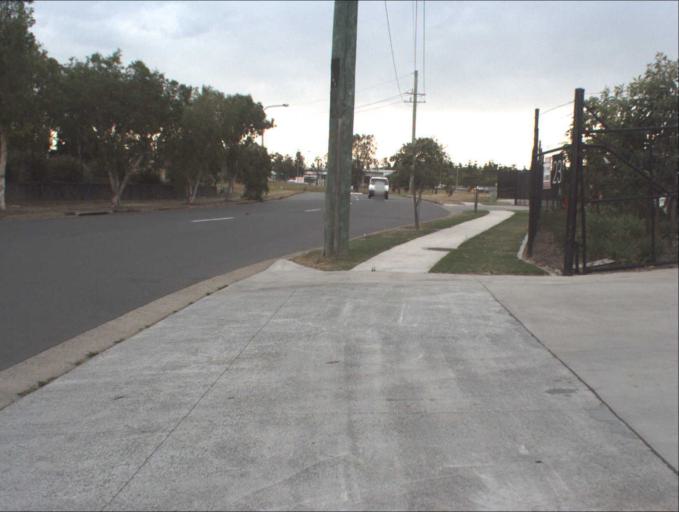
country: AU
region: Queensland
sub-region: Logan
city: Beenleigh
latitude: -27.6818
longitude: 153.1902
